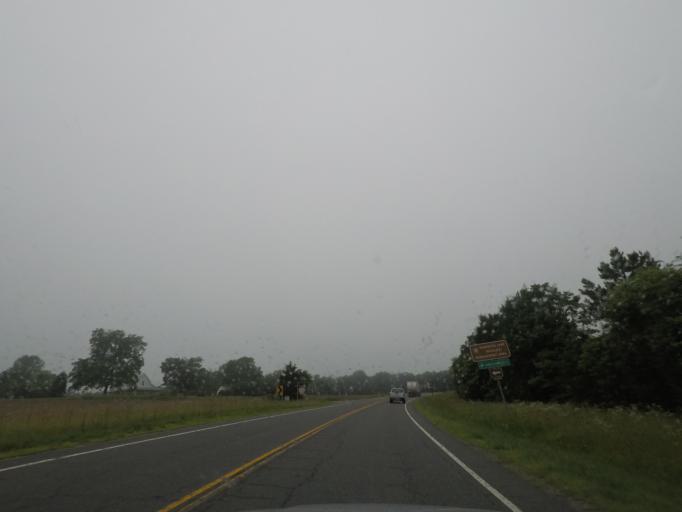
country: US
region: Virginia
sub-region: Buckingham County
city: Buckingham
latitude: 37.5196
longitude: -78.4948
